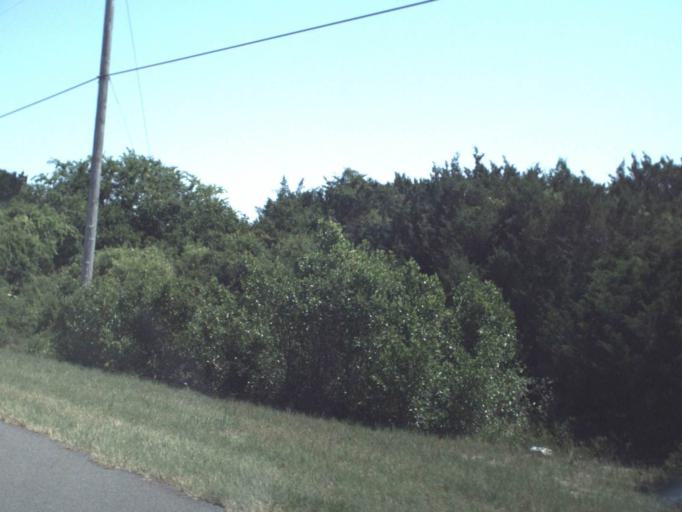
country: US
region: Florida
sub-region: Duval County
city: Atlantic Beach
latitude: 30.4553
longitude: -81.4163
